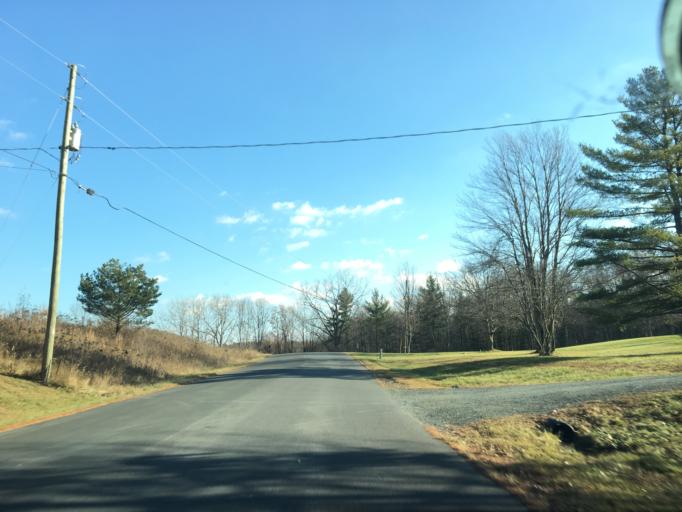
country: US
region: New York
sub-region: Rensselaer County
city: West Sand Lake
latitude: 42.6030
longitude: -73.5924
